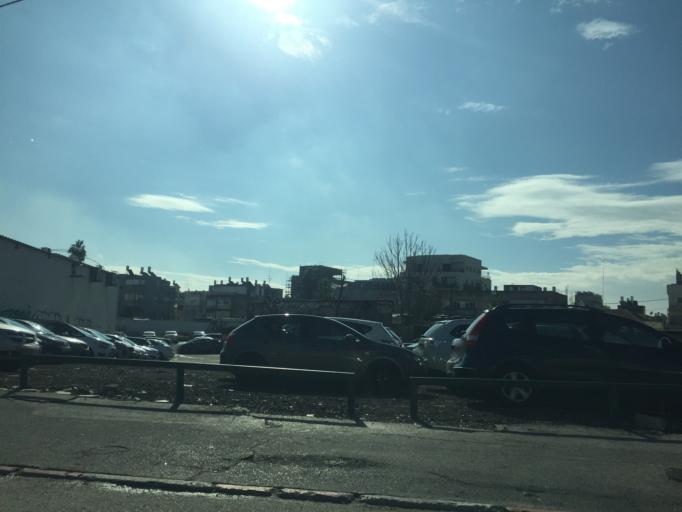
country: IL
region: Tel Aviv
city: Tel Aviv
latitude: 32.0606
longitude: 34.7765
